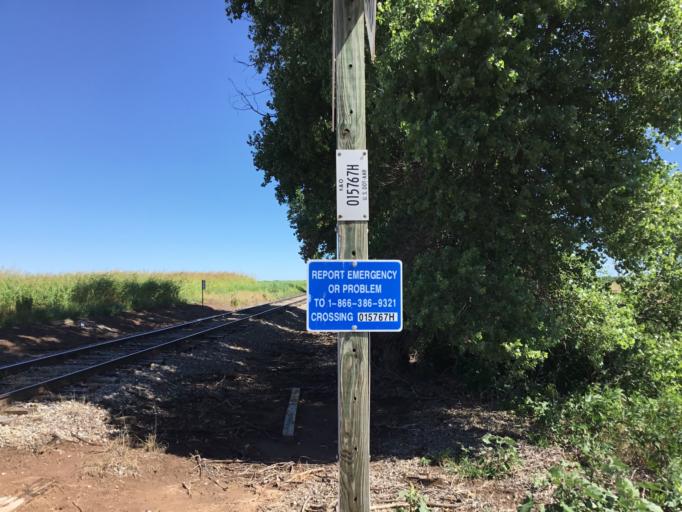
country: US
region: Kansas
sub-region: Kingman County
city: Kingman
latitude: 37.4870
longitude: -98.0906
